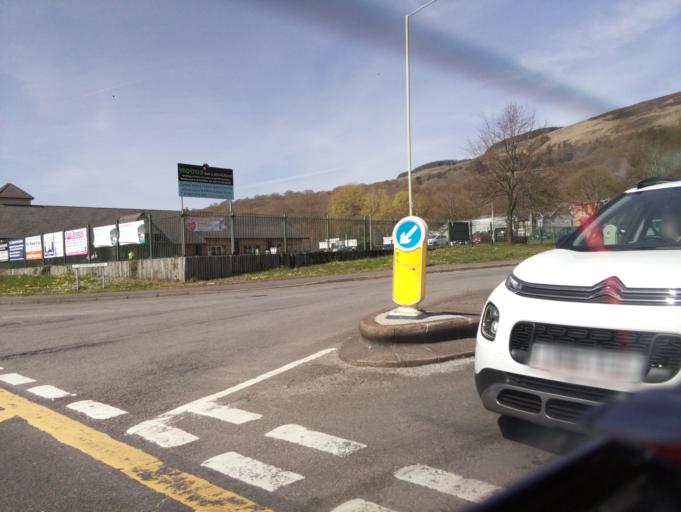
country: GB
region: Wales
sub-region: Rhondda Cynon Taf
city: Mountain Ash
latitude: 51.6854
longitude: -3.3808
